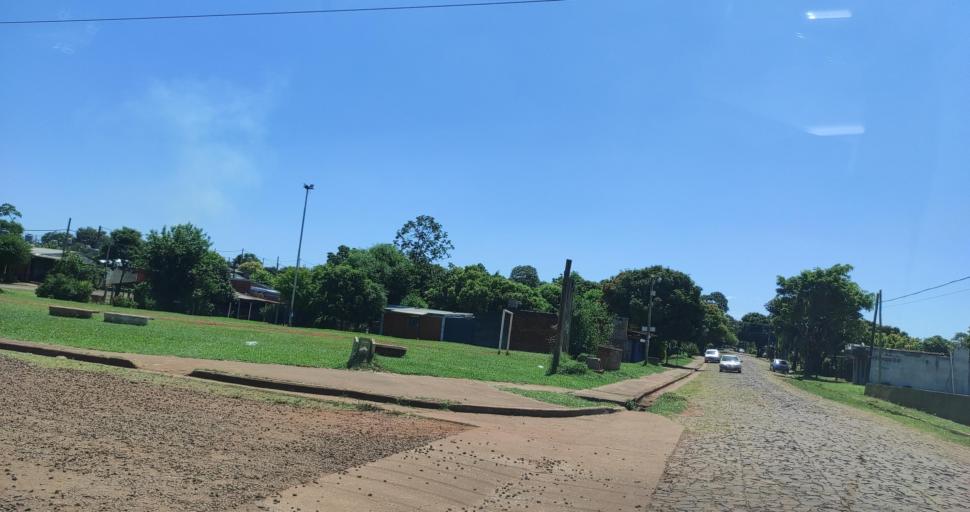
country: AR
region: Misiones
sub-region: Departamento de Capital
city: Posadas
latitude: -27.4130
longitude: -55.9082
